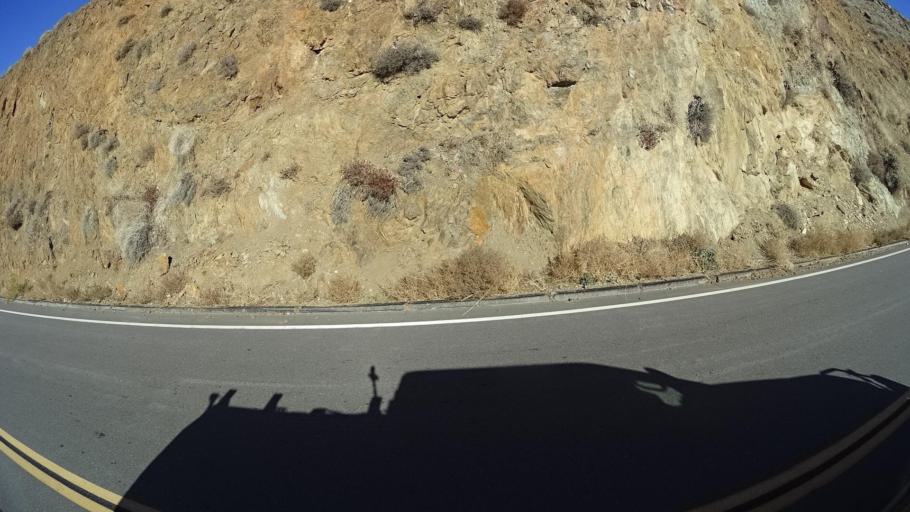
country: US
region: California
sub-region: Kern County
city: Wofford Heights
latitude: 35.6778
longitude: -118.4172
